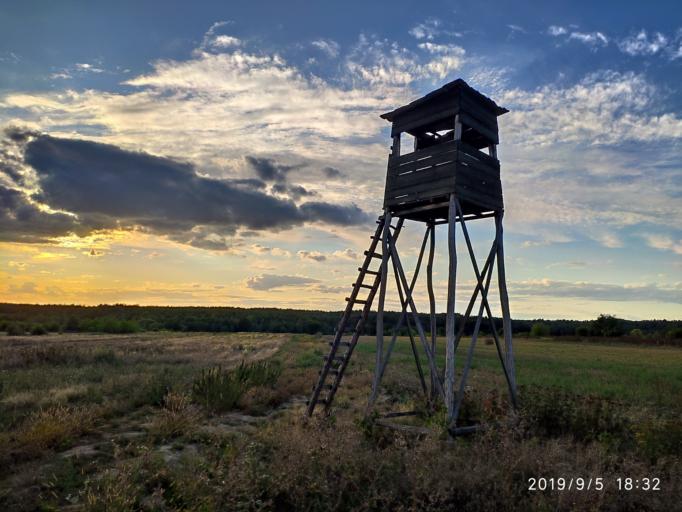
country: PL
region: Lubusz
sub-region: Powiat krosnienski
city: Dabie
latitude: 52.0193
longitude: 15.2124
